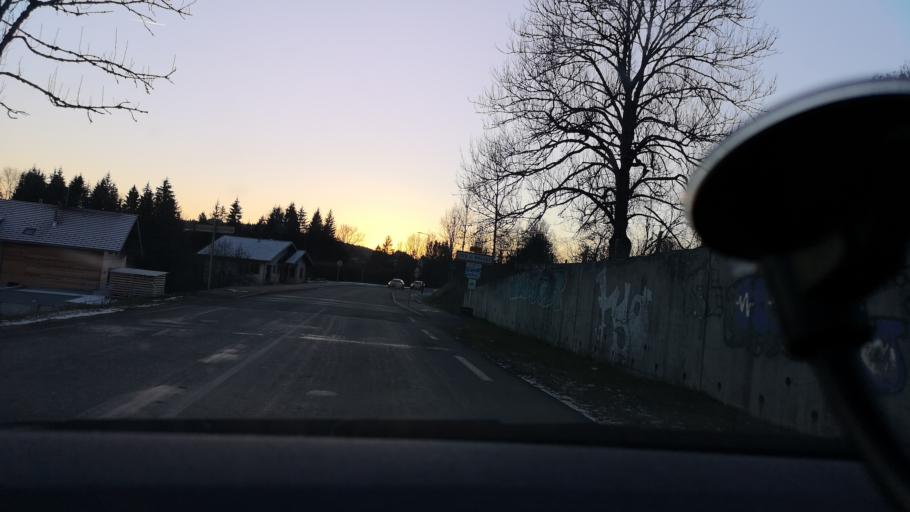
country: FR
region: Franche-Comte
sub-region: Departement du Doubs
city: Pontarlier
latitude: 46.8587
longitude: 6.3418
